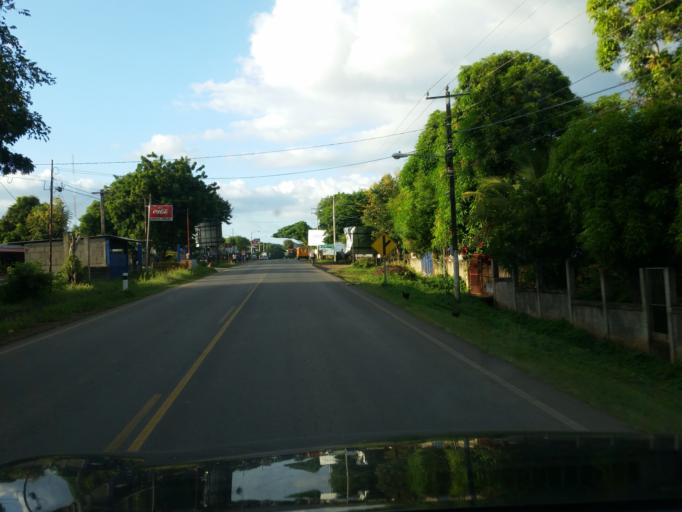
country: NI
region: Granada
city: Nandaime
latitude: 11.7750
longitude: -86.0525
